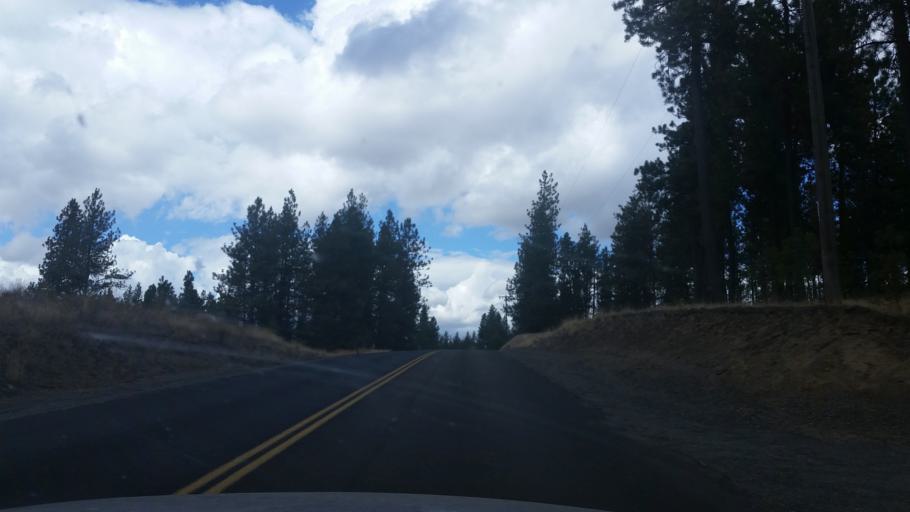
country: US
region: Washington
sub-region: Spokane County
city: Spokane
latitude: 47.5622
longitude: -117.4890
